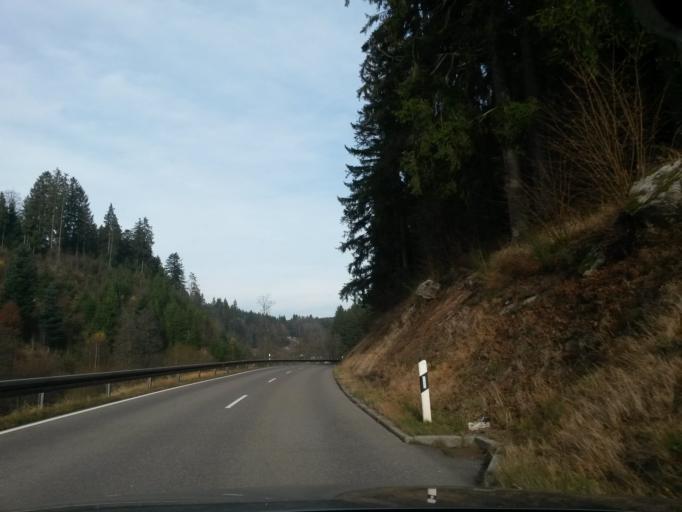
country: DE
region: Baden-Wuerttemberg
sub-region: Freiburg Region
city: Tennenbronn
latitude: 48.1632
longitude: 8.3273
